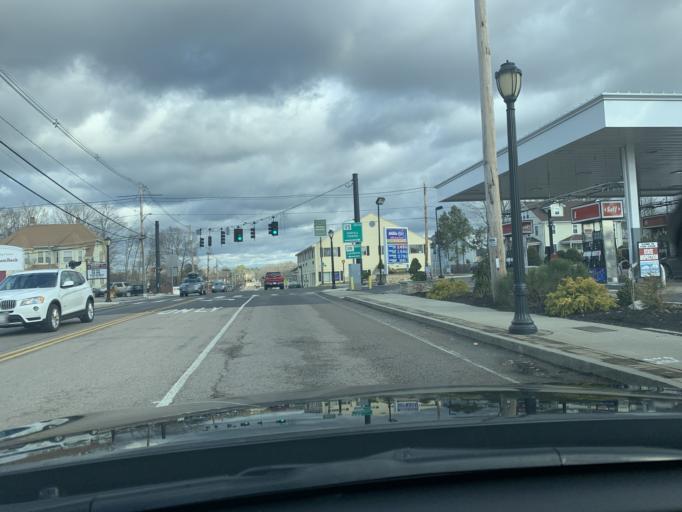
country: US
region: Massachusetts
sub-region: Norfolk County
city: Millis
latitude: 42.1675
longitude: -71.3585
